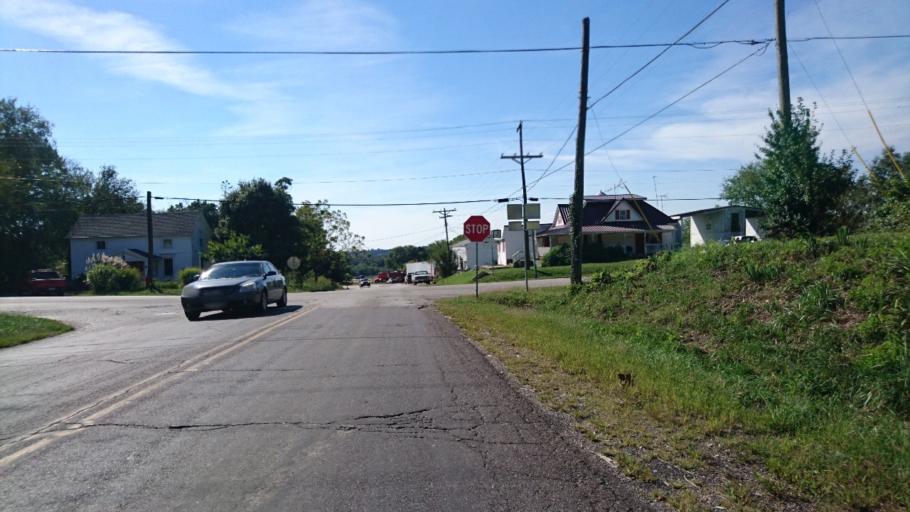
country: US
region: Missouri
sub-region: Crawford County
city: Bourbon
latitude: 38.1577
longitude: -91.2435
